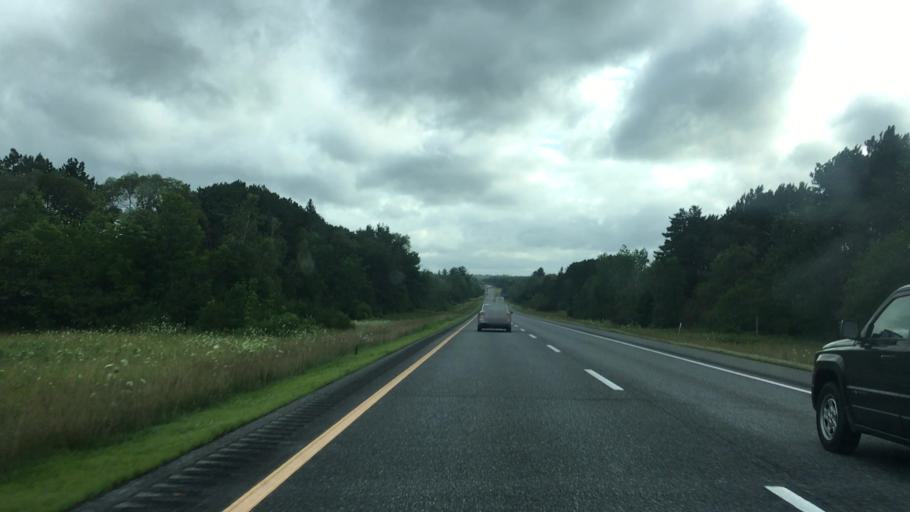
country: US
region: Maine
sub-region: Kennebec County
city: Clinton
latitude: 44.6606
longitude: -69.5004
